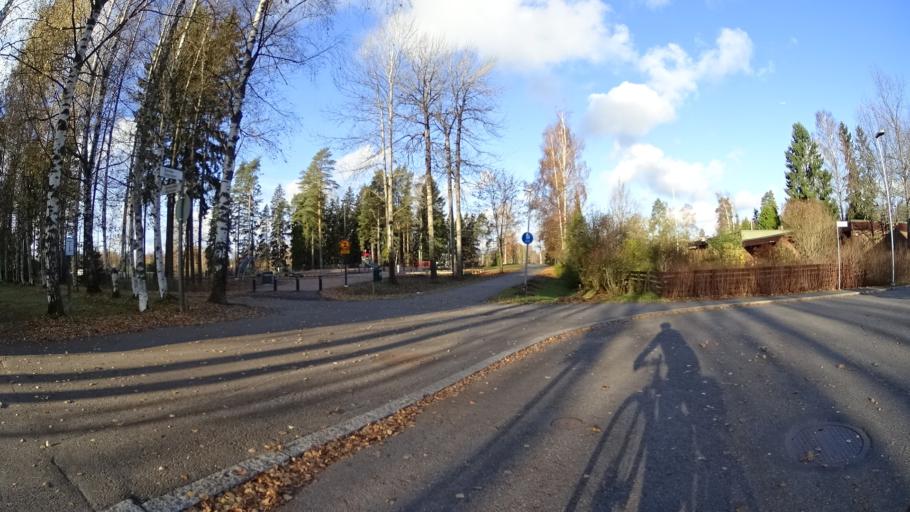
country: FI
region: Uusimaa
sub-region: Helsinki
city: Kilo
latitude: 60.2600
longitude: 24.8289
